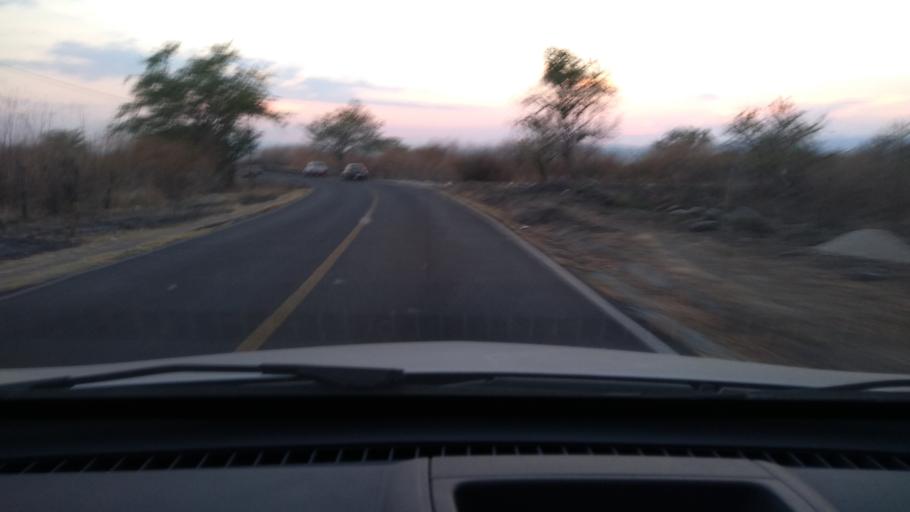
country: MX
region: Morelos
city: Coatetelco
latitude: 18.7244
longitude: -99.3002
